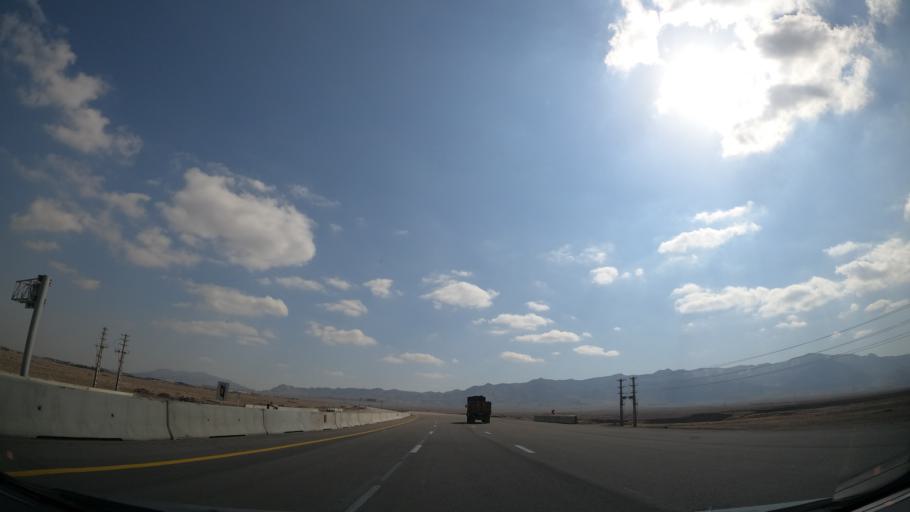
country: IR
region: Alborz
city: Eshtehard
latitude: 35.7276
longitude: 50.5625
